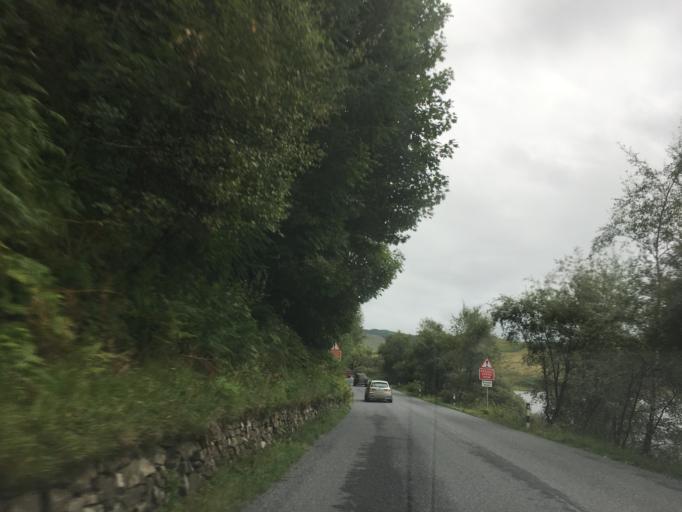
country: GB
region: Scotland
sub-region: Argyll and Bute
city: Oban
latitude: 56.2699
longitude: -5.4792
